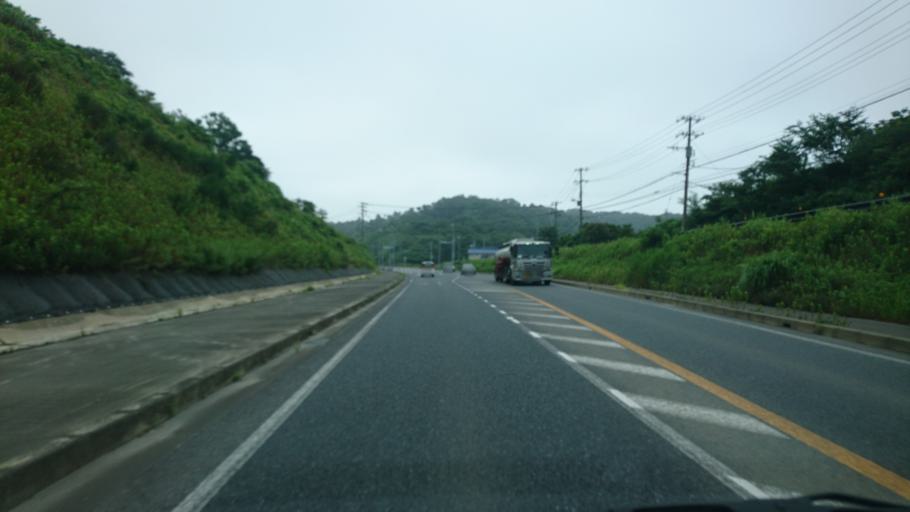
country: JP
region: Chiba
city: Kimitsu
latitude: 35.2541
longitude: 139.8842
